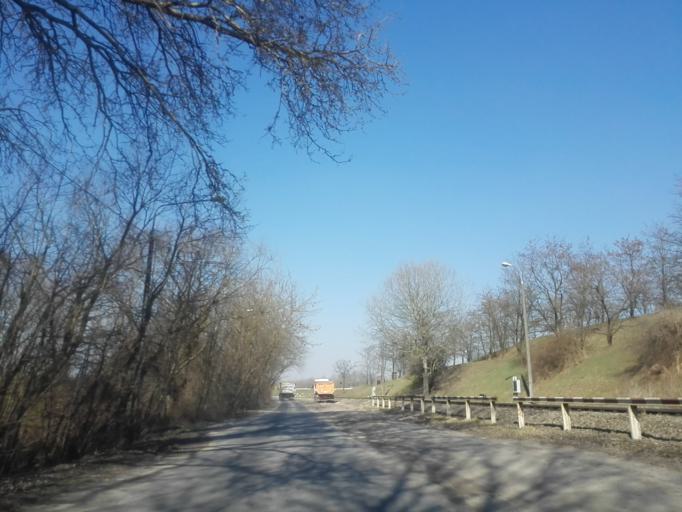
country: PL
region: Masovian Voivodeship
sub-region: Warszawa
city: Wilanow
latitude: 52.1586
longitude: 21.1363
